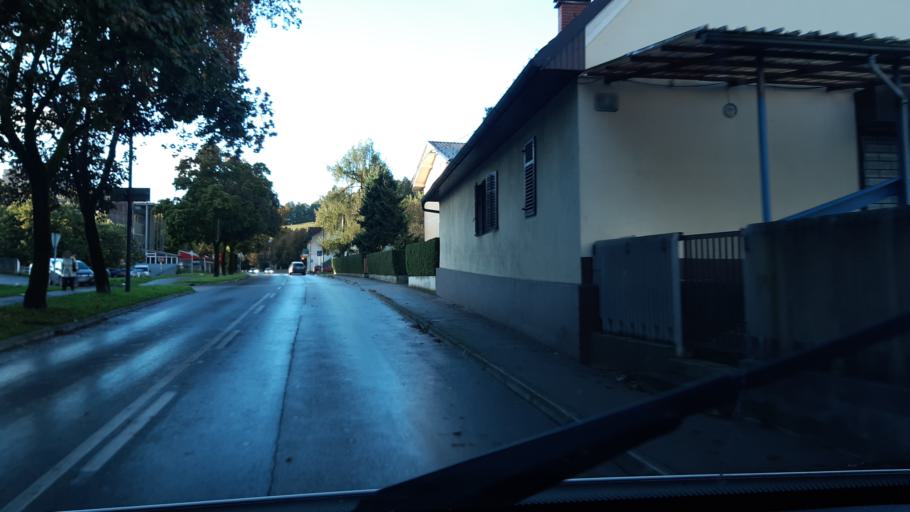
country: SI
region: Ljubljana
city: Ljubljana
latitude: 46.0494
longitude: 14.5430
